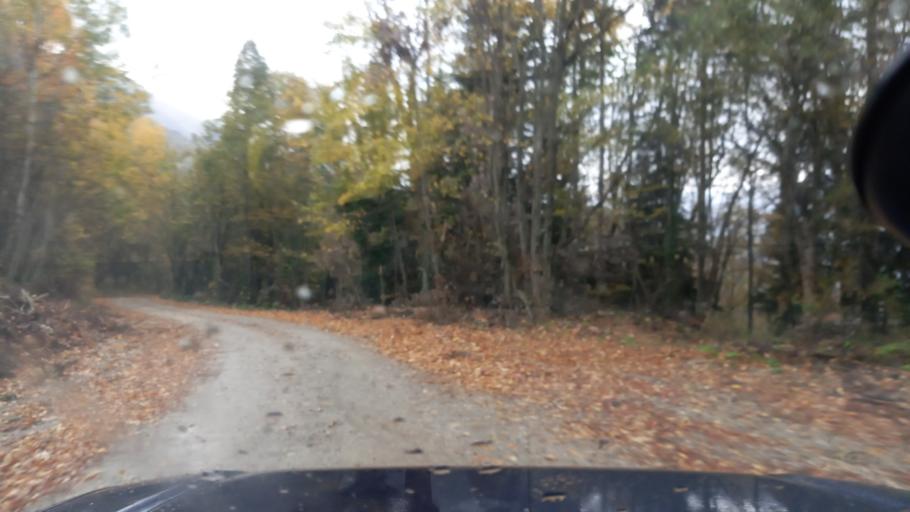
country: RU
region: Krasnodarskiy
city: Neftegorsk
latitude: 44.0491
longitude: 39.8291
